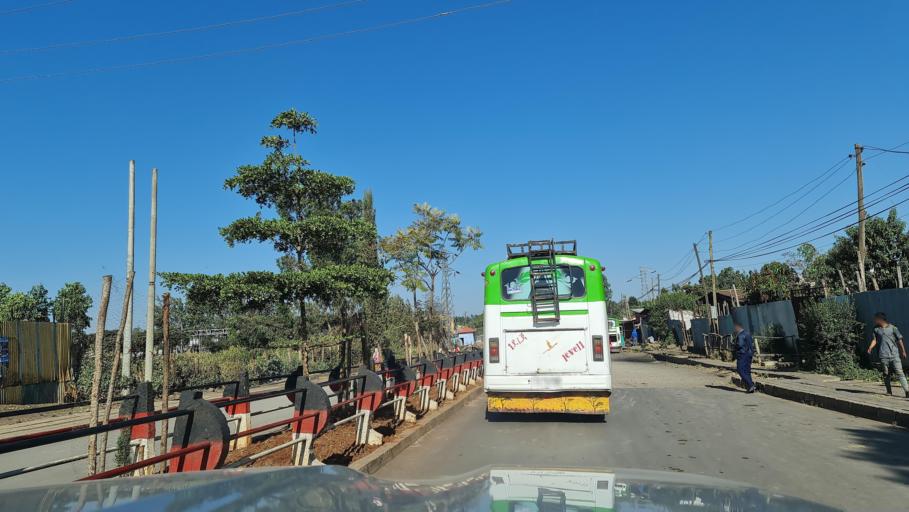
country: ET
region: Oromiya
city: Waliso
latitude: 8.5431
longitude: 37.9697
